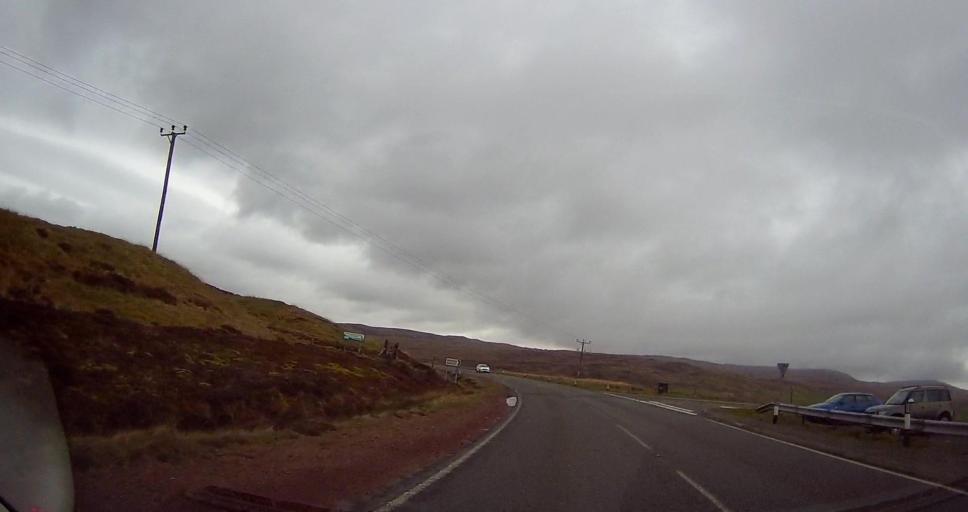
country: GB
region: Scotland
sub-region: Shetland Islands
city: Lerwick
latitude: 60.2638
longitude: -1.2221
